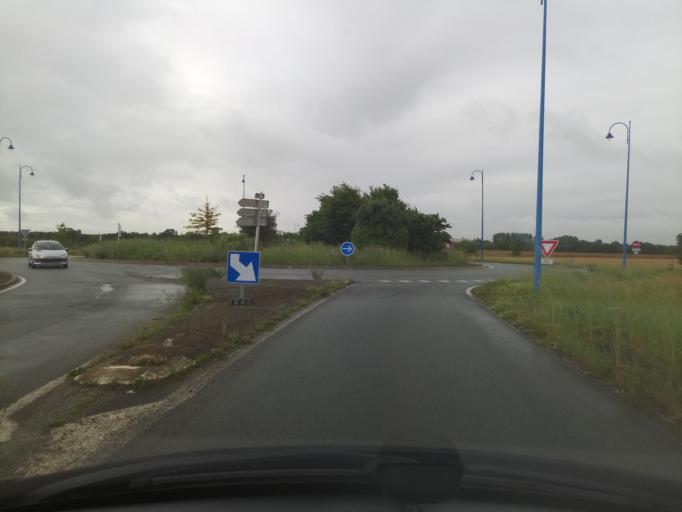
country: FR
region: Poitou-Charentes
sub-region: Departement de la Charente-Maritime
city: Saint-Jean-de-Liversay
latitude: 46.1958
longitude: -0.8687
